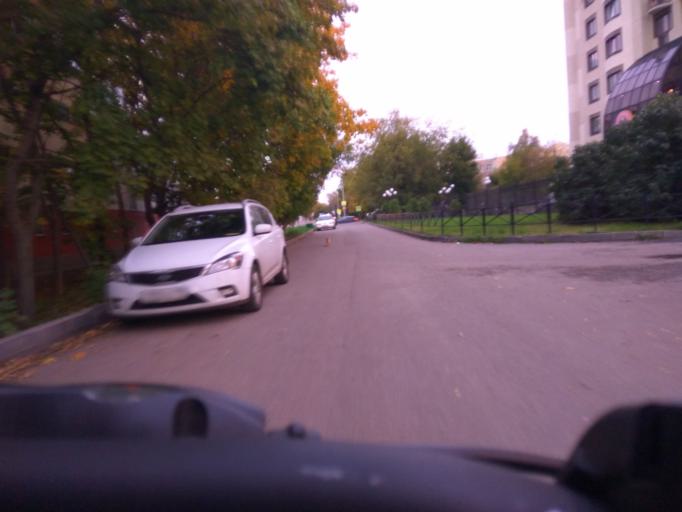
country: RU
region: Moscow
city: Golovinskiy
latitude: 55.8522
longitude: 37.4930
